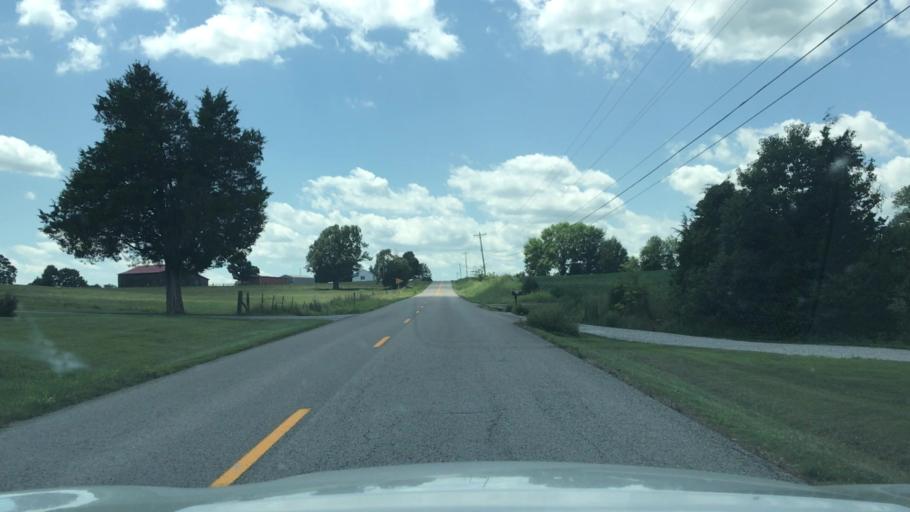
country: US
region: Kentucky
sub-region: Christian County
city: Hopkinsville
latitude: 36.9700
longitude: -87.3762
